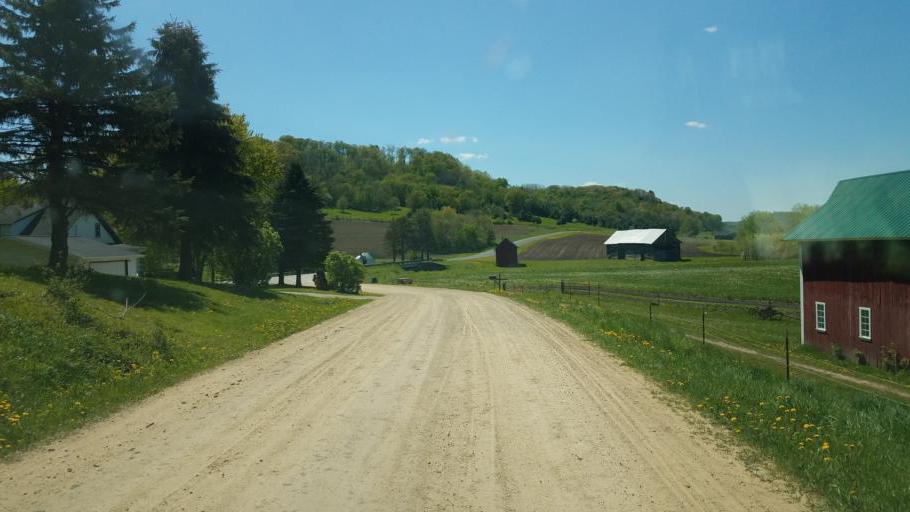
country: US
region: Wisconsin
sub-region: Vernon County
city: Hillsboro
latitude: 43.5652
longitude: -90.4177
